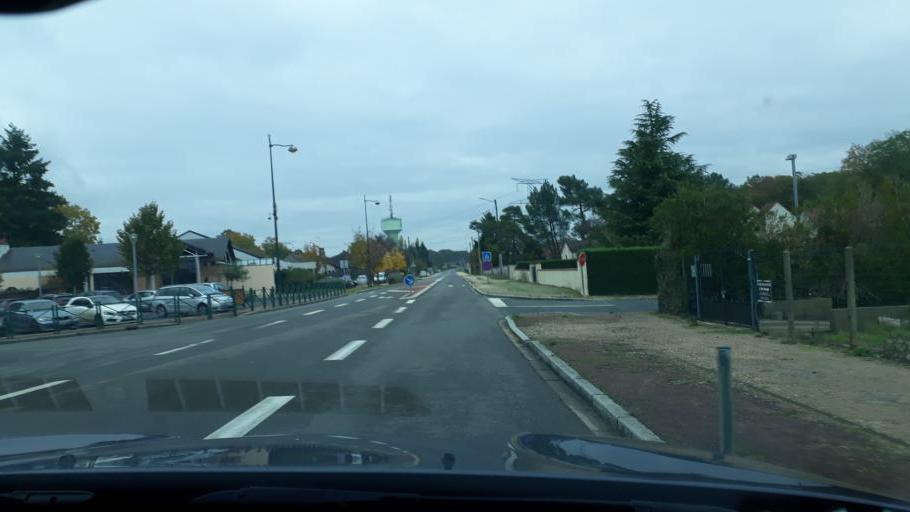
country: FR
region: Centre
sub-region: Departement du Loiret
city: Bray-en-Val
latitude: 47.8174
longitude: 2.4057
